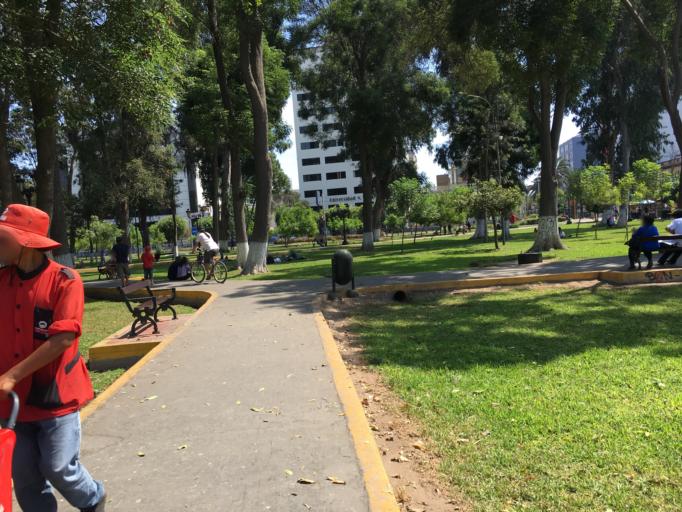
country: PE
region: Lima
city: Lima
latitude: -12.0685
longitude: -77.0359
